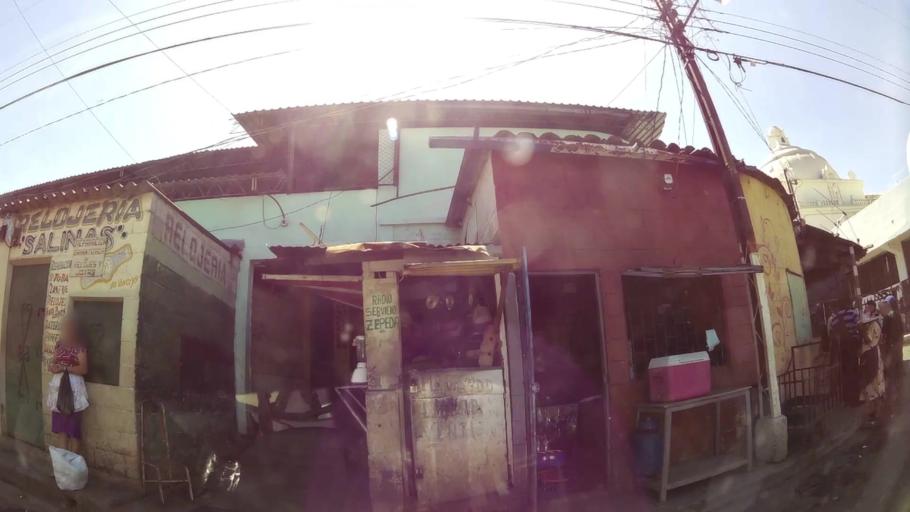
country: SV
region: Ahuachapan
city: Atiquizaya
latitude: 13.9771
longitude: -89.7556
